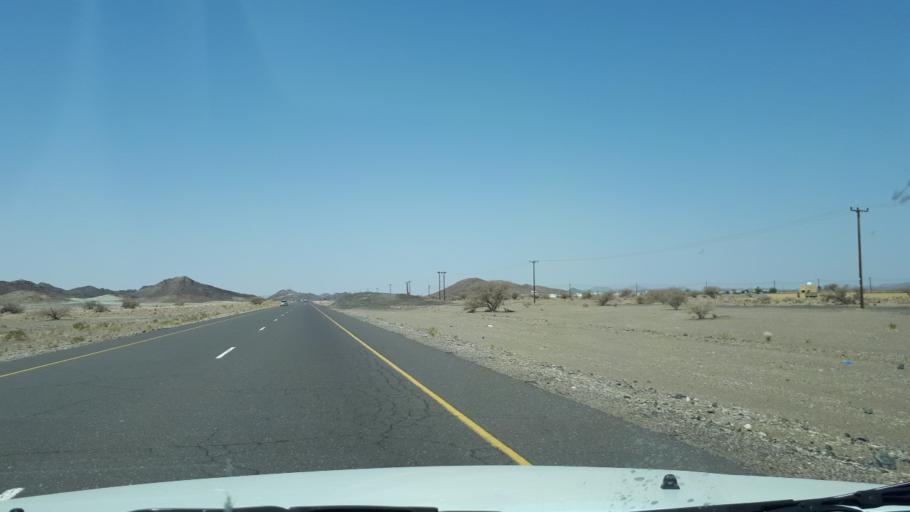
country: OM
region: Ash Sharqiyah
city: Ibra'
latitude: 22.6386
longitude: 58.4803
